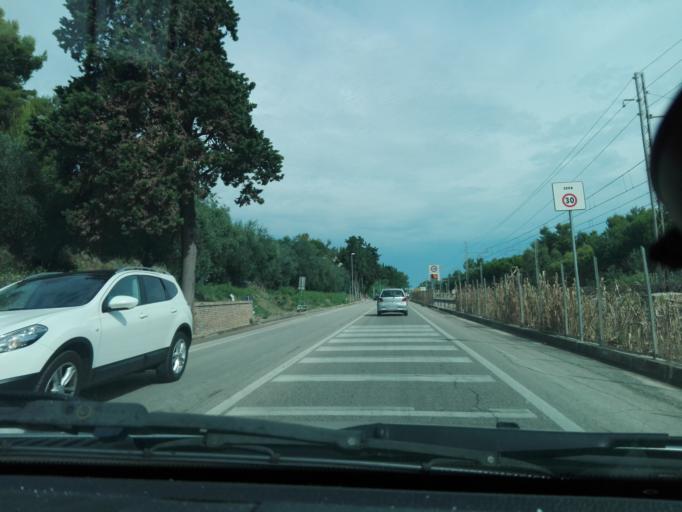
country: IT
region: Abruzzo
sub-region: Provincia di Teramo
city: Pineto
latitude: 42.5886
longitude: 14.0849
